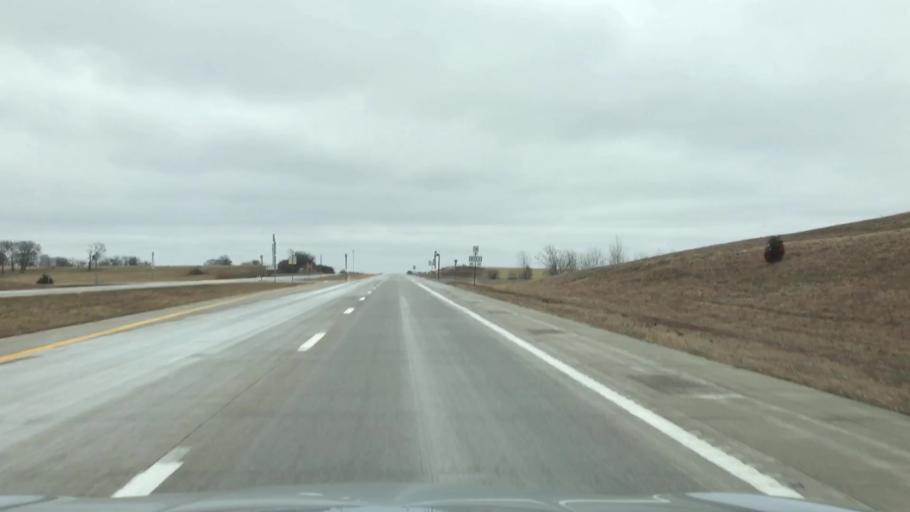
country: US
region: Missouri
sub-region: Caldwell County
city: Hamilton
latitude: 39.7349
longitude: -93.7975
